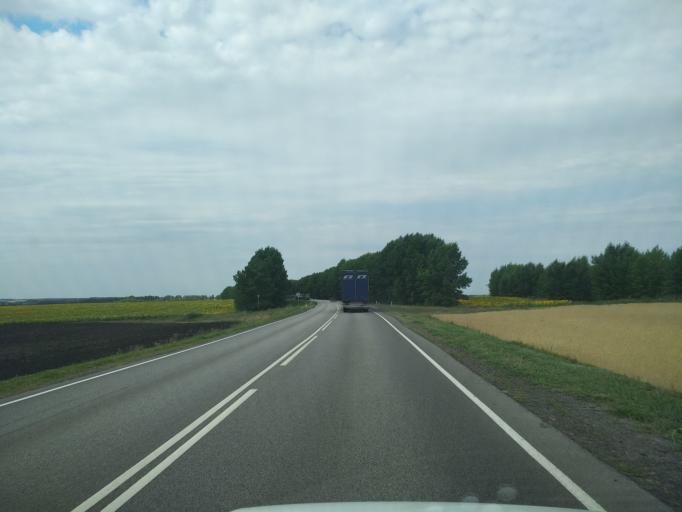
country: RU
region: Voronezj
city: Pereleshinskiy
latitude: 51.8496
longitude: 40.3171
